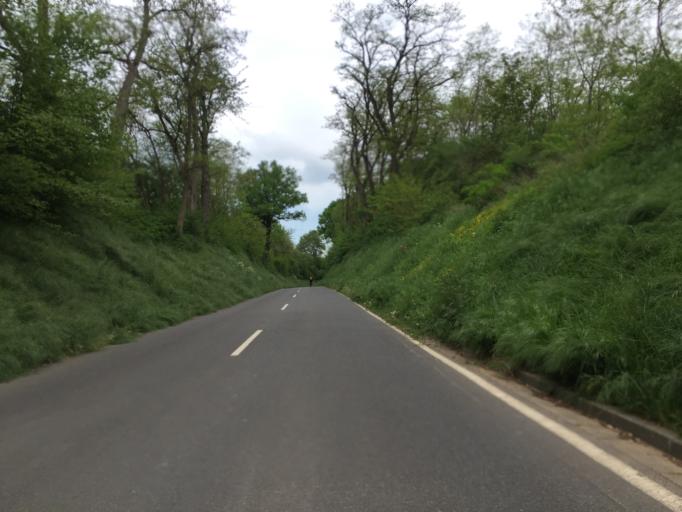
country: DE
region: Bavaria
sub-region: Regierungsbezirk Unterfranken
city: Hosbach
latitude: 50.0113
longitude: 9.2080
